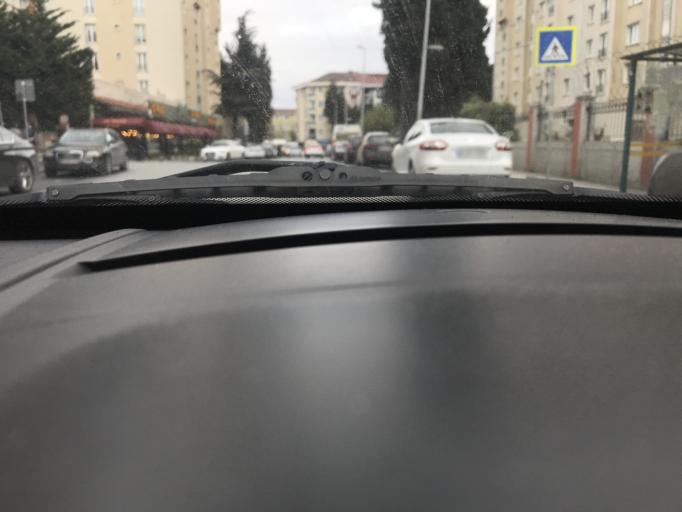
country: TR
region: Istanbul
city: Yakuplu
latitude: 41.0032
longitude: 28.6934
